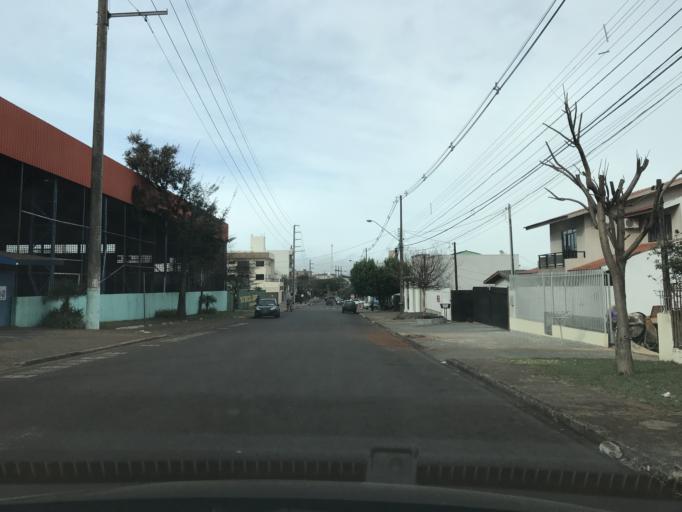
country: BR
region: Parana
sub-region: Cascavel
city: Cascavel
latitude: -24.9543
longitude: -53.4816
